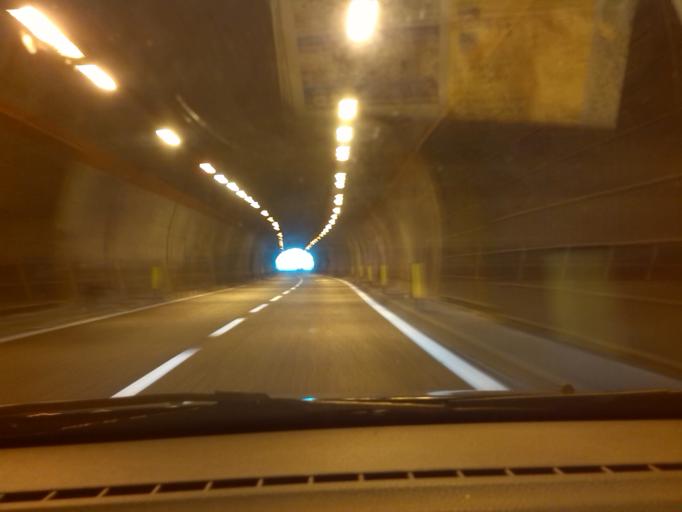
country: IT
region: Friuli Venezia Giulia
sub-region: Provincia di Trieste
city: Trieste
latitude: 45.6243
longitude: 13.7809
